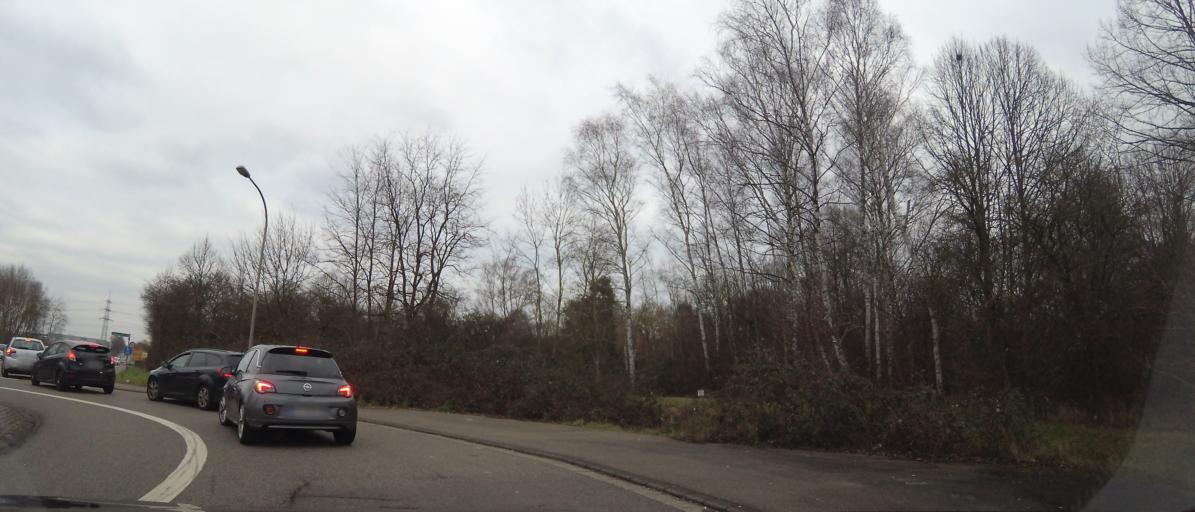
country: DE
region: Saarland
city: Ensdorf
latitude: 49.2867
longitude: 6.7847
